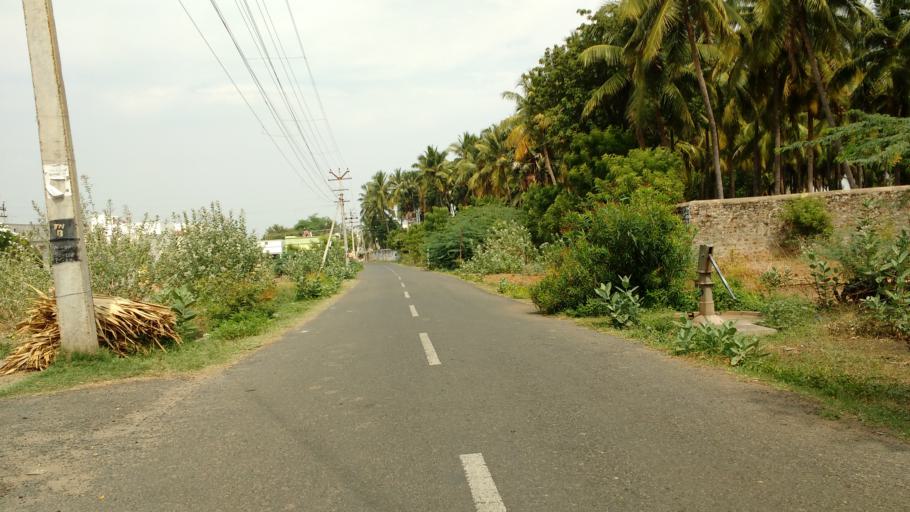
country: IN
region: Tamil Nadu
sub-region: Erode
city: Gobichettipalayam
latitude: 11.4516
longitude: 77.4455
